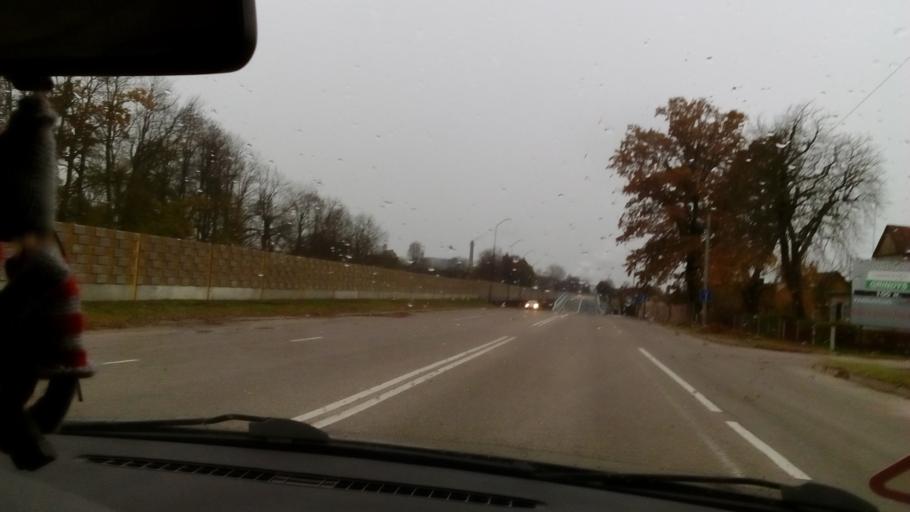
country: LT
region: Marijampoles apskritis
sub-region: Marijampole Municipality
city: Marijampole
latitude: 54.5466
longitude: 23.3571
